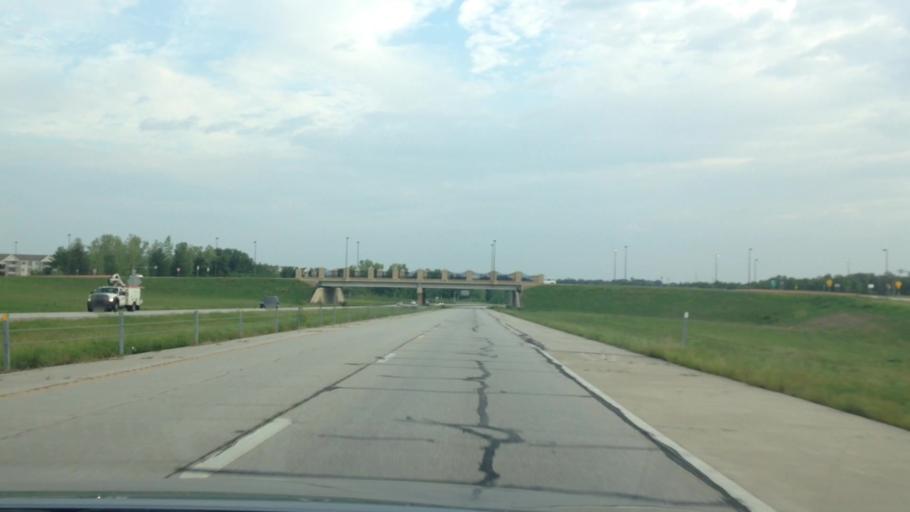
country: US
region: Missouri
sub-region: Clay County
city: Gladstone
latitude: 39.2724
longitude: -94.5850
